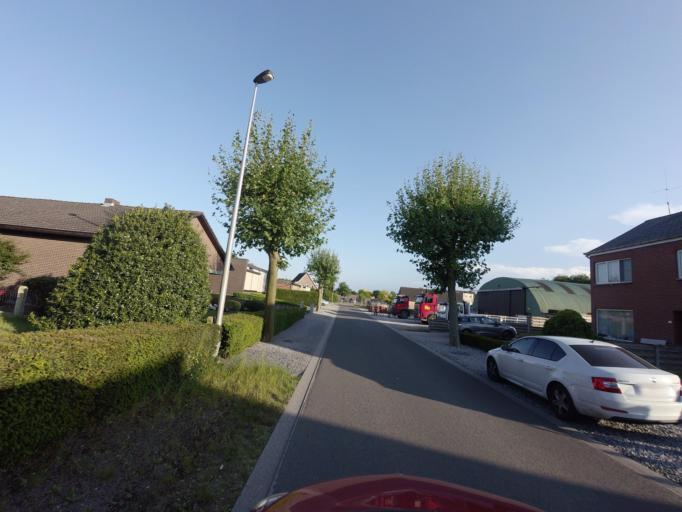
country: BE
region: Flanders
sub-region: Provincie Limburg
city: Lommel
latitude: 51.2329
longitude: 5.3404
